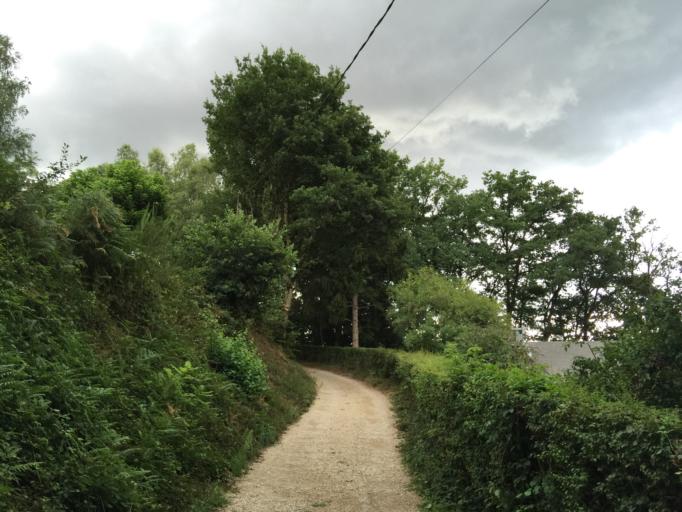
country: FR
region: Midi-Pyrenees
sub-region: Departement de l'Aveyron
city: Pont-de-Salars
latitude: 44.3039
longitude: 2.7355
